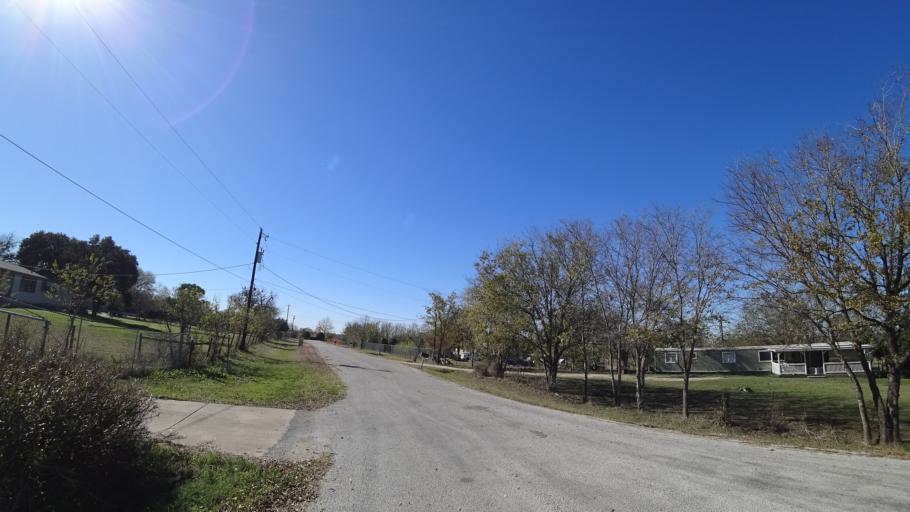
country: US
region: Texas
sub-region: Travis County
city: Garfield
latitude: 30.1091
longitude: -97.5948
